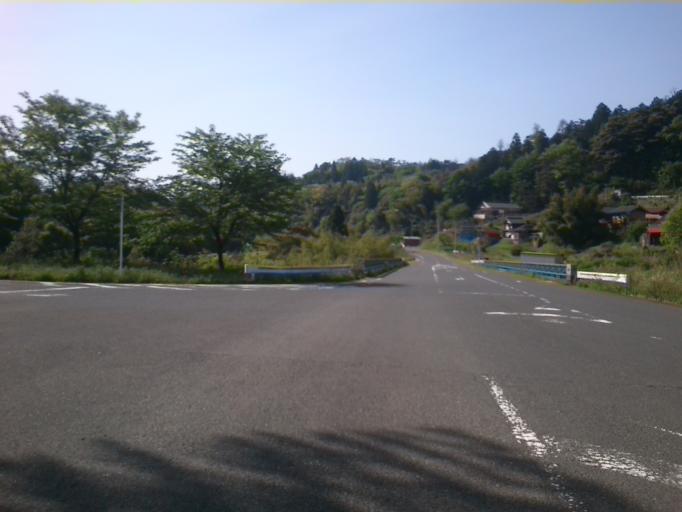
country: JP
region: Kyoto
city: Miyazu
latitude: 35.6326
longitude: 135.2124
